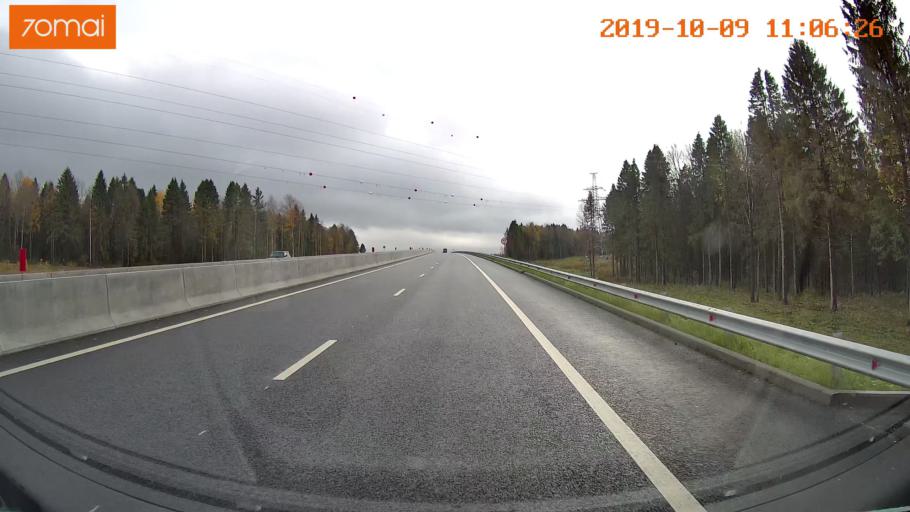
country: RU
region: Vologda
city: Vologda
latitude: 59.1866
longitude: 39.7605
